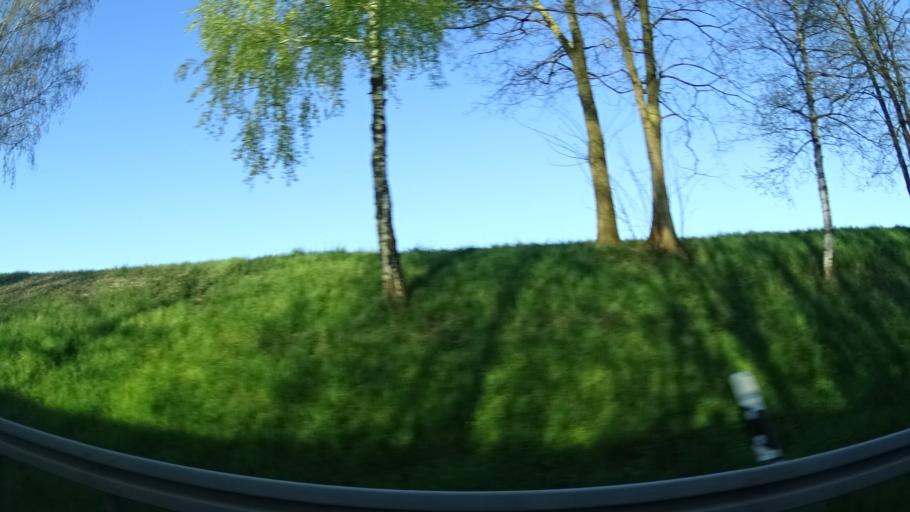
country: DE
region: Baden-Wuerttemberg
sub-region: Regierungsbezirk Stuttgart
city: Kupferzell
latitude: 49.2115
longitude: 9.6790
